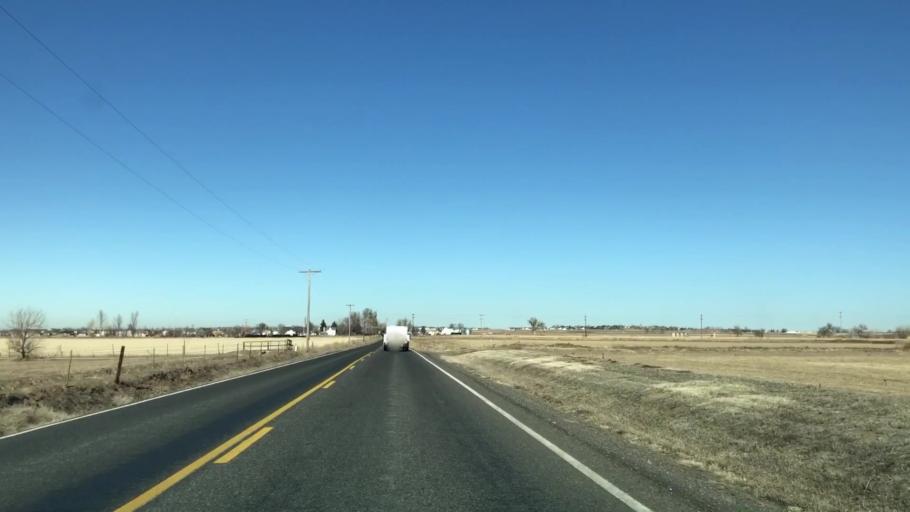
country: US
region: Colorado
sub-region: Weld County
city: Windsor
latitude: 40.5004
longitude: -104.9441
